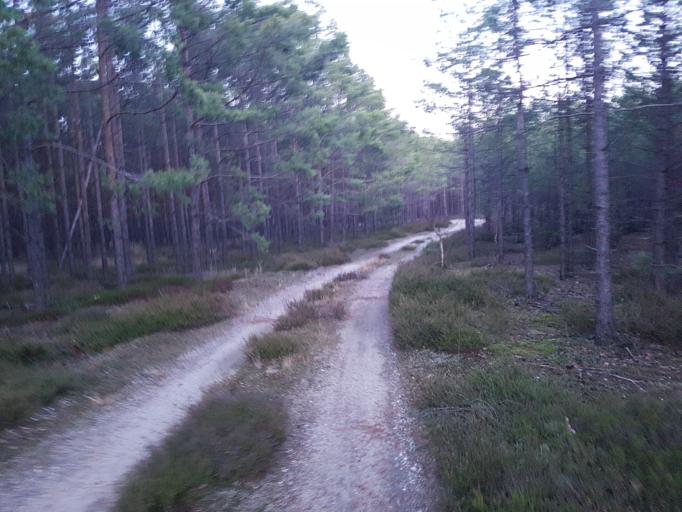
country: DE
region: Brandenburg
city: Schonewalde
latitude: 51.6367
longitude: 13.6334
